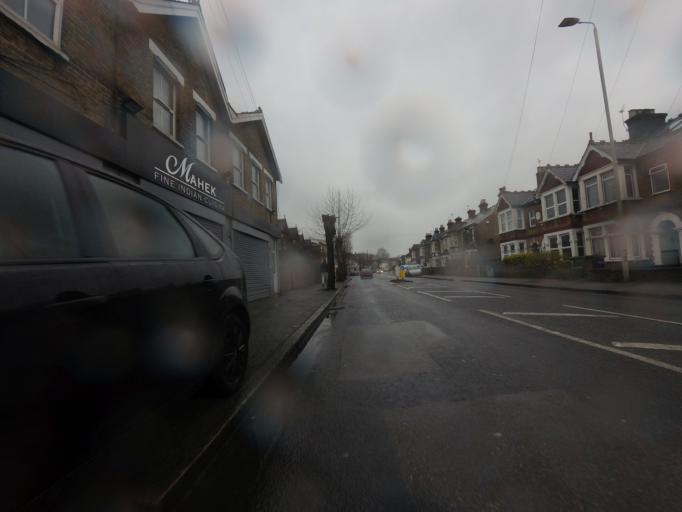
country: GB
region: England
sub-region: Hertfordshire
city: Cheshunt
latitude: 51.7057
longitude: -0.0350
